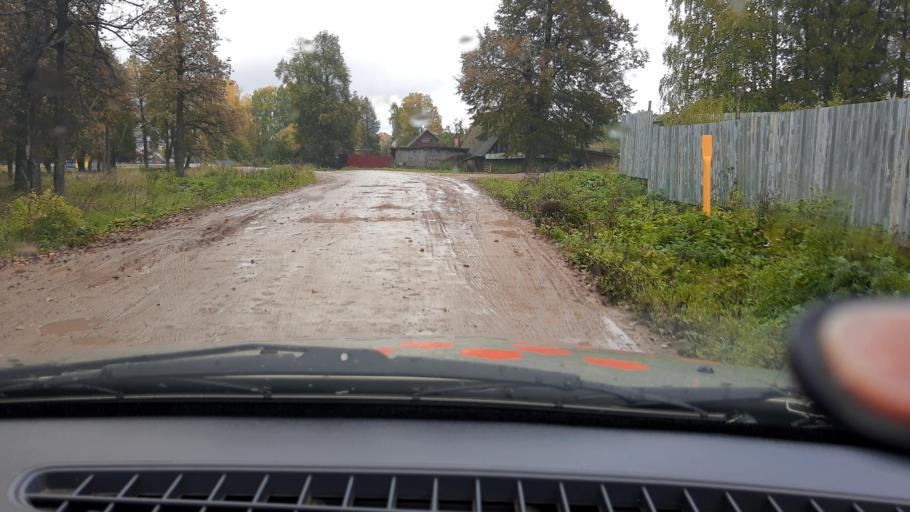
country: RU
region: Bashkortostan
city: Kudeyevskiy
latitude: 54.8803
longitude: 56.6330
